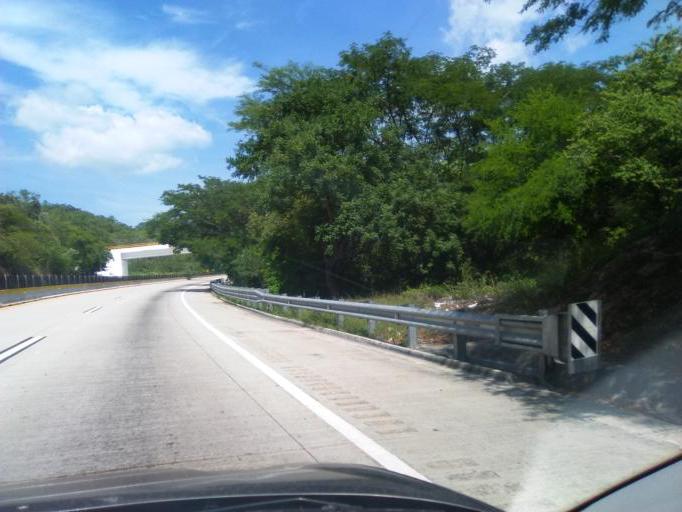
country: MX
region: Guerrero
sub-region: Acapulco de Juarez
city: Colonia Nueva Revolucion
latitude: 16.9396
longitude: -99.7820
